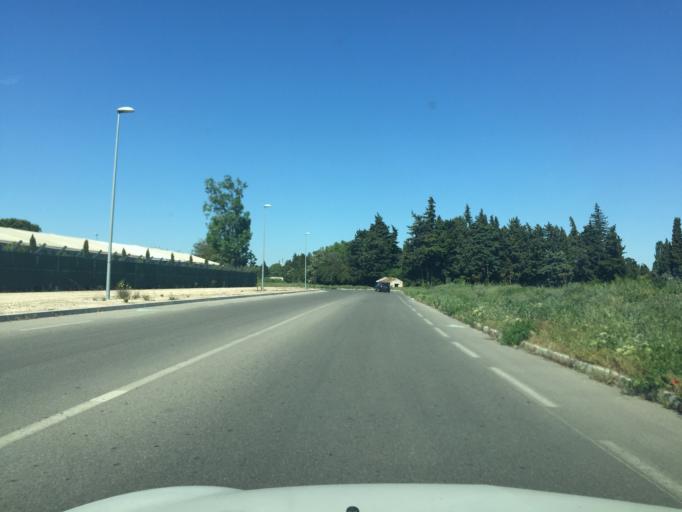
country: FR
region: Provence-Alpes-Cote d'Azur
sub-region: Departement du Vaucluse
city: Montfavet
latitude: 43.9255
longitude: 4.8568
